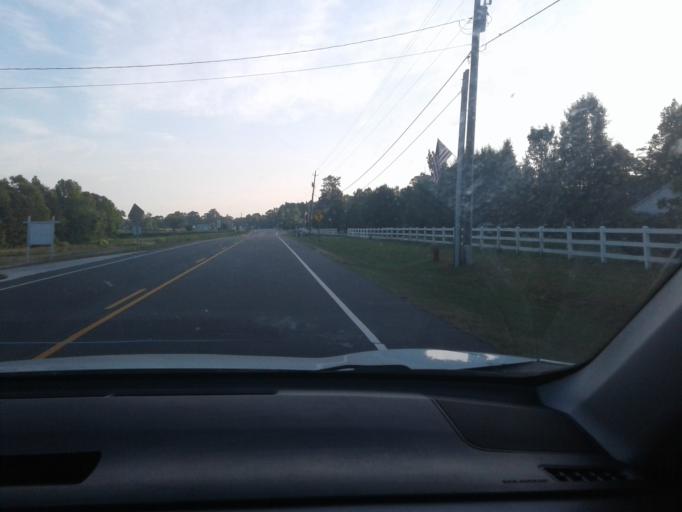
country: US
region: North Carolina
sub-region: Harnett County
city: Angier
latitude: 35.4933
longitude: -78.8151
